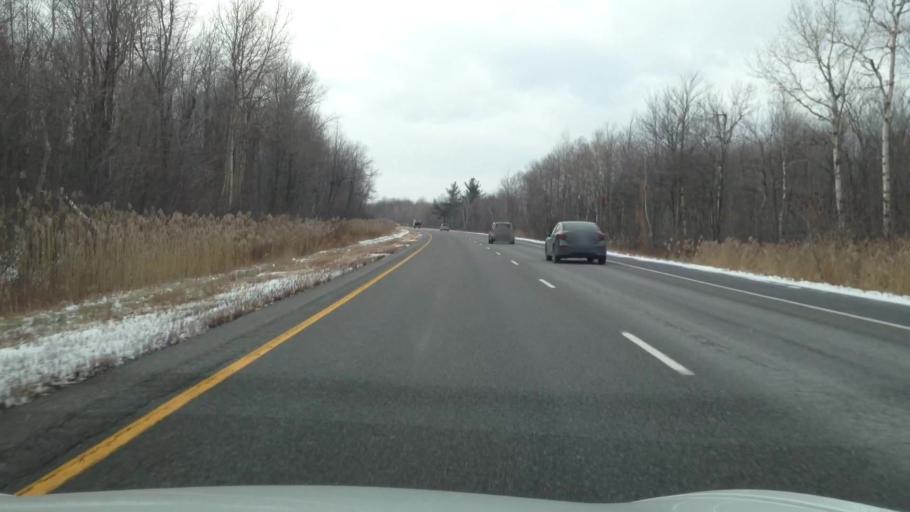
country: CA
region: Ontario
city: Casselman
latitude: 45.3059
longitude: -75.1096
